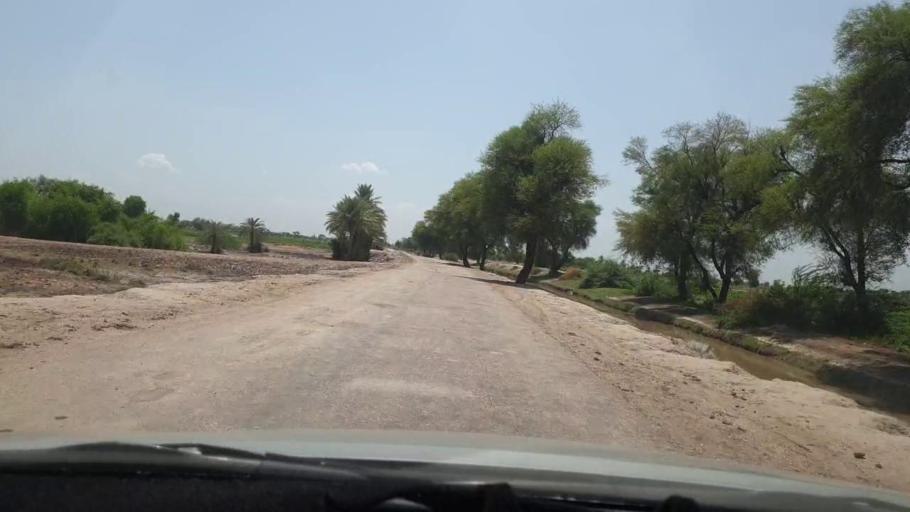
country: PK
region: Sindh
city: Pano Aqil
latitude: 27.7340
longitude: 69.1888
